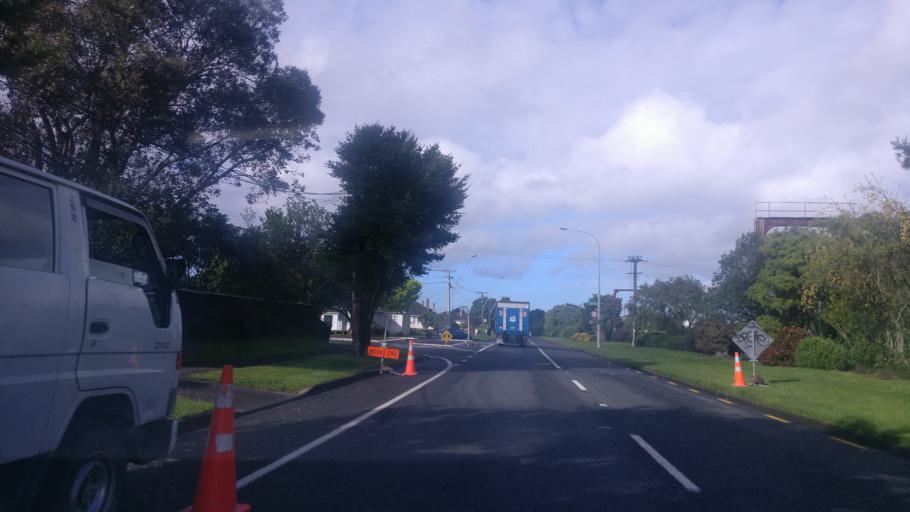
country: NZ
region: Wellington
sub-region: Lower Hutt City
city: Lower Hutt
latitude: -41.2048
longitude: 174.9350
